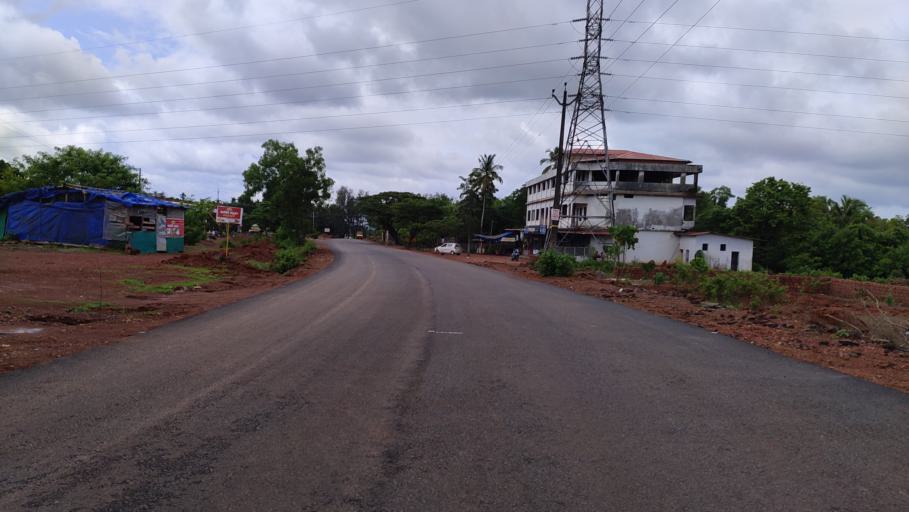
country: IN
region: Kerala
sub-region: Kasaragod District
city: Kasaragod
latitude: 12.5430
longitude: 75.0703
